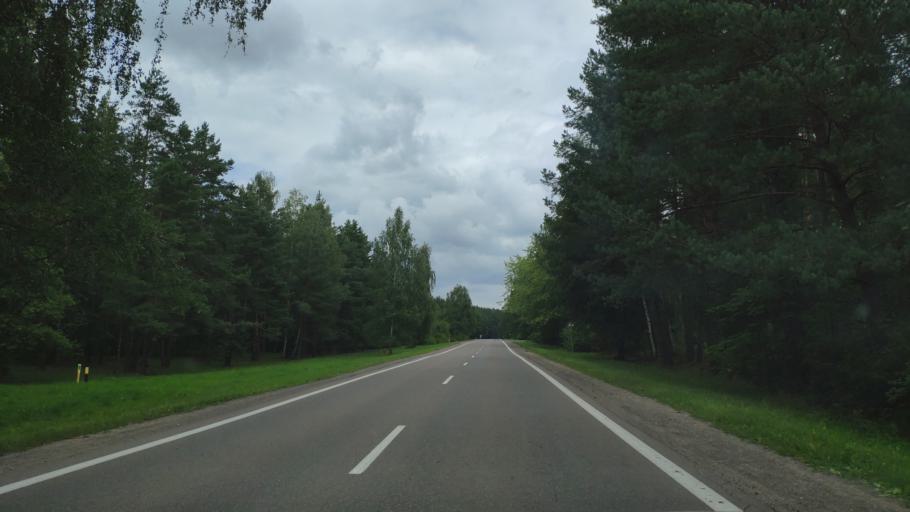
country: BY
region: Minsk
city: Zhdanovichy
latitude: 53.9743
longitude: 27.4380
